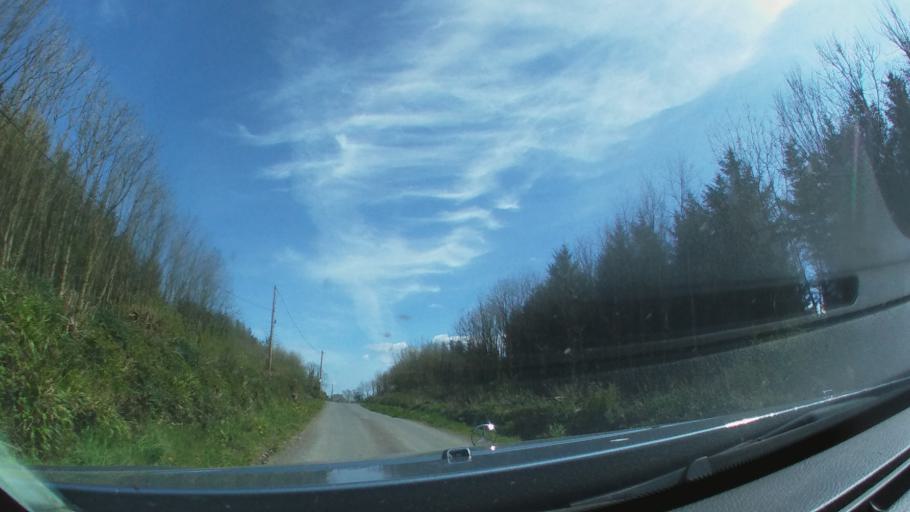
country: IE
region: Leinster
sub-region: Kilkenny
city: Callan
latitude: 52.6197
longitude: -7.5025
